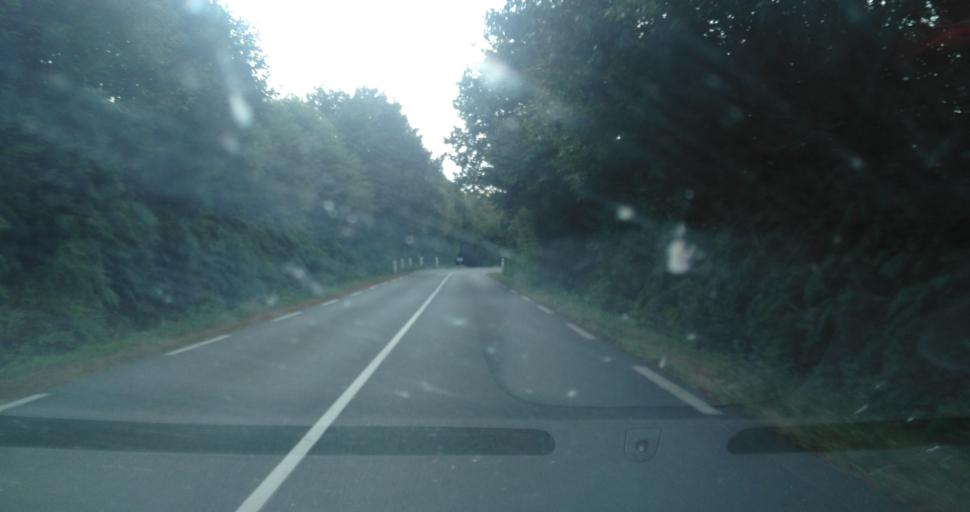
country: FR
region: Pays de la Loire
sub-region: Departement de la Vendee
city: Bournezeau
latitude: 46.5948
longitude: -1.1257
